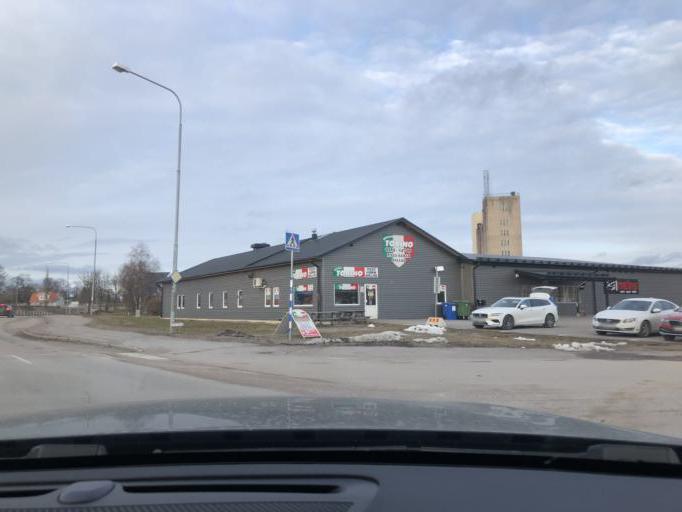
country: SE
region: Uppsala
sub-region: Tierps Kommun
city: Tierp
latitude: 60.3405
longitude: 17.5191
